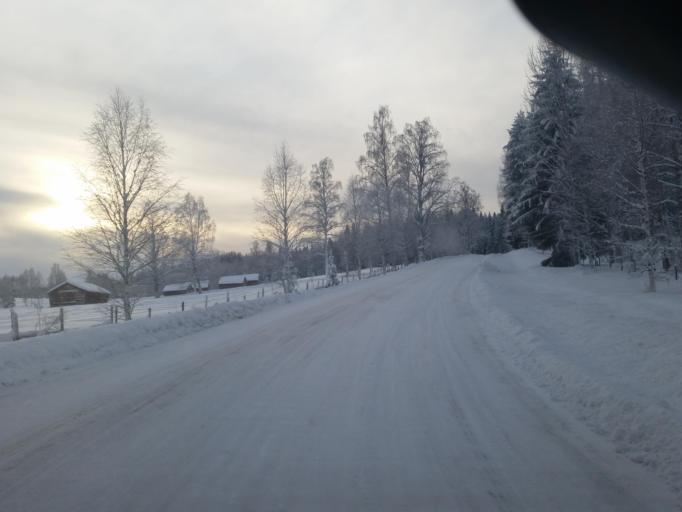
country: SE
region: Norrbotten
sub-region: Pitea Kommun
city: Norrfjarden
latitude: 65.5731
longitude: 21.4856
